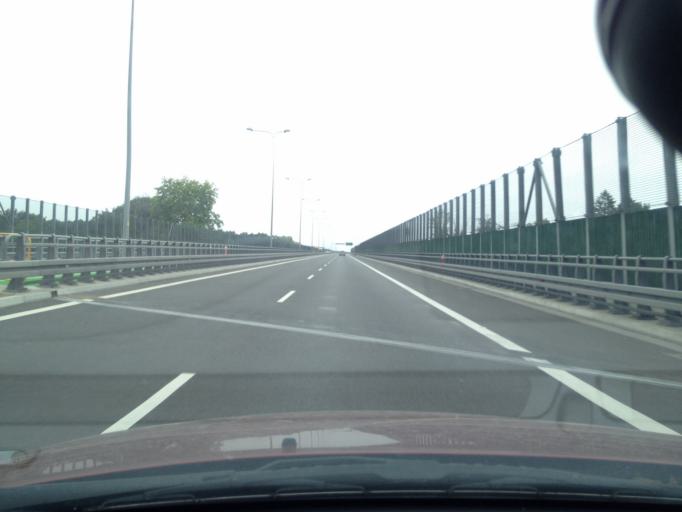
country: PL
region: Lubusz
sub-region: Powiat miedzyrzecki
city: Skwierzyna
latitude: 52.5832
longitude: 15.4574
